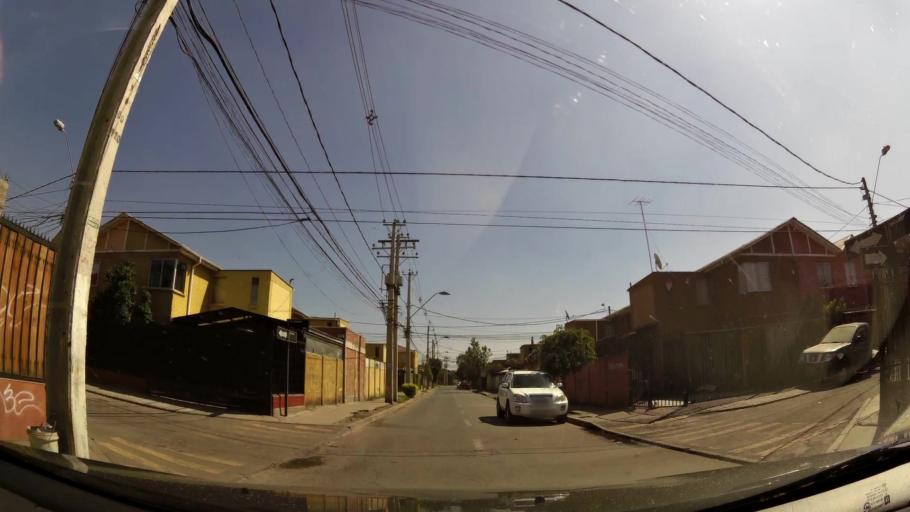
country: CL
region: Santiago Metropolitan
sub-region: Provincia de Santiago
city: Lo Prado
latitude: -33.3542
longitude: -70.7167
